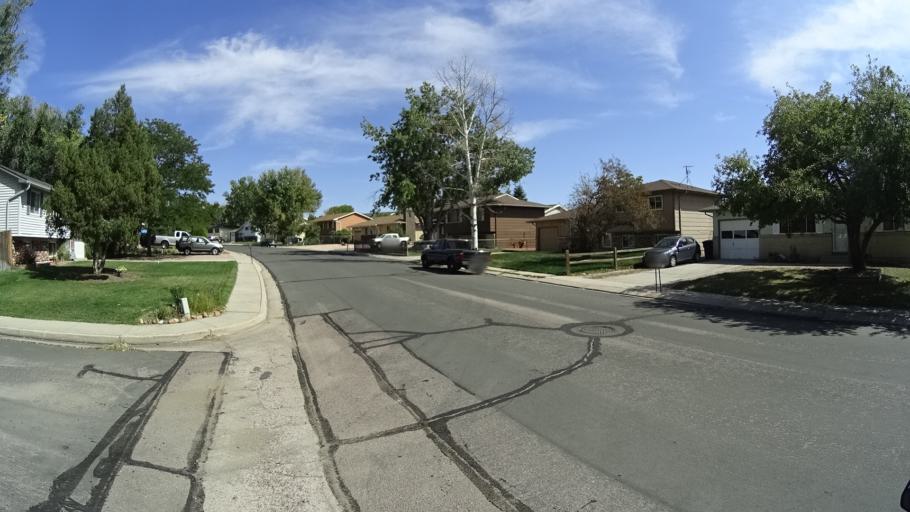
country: US
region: Colorado
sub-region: El Paso County
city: Cimarron Hills
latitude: 38.8964
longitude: -104.7569
